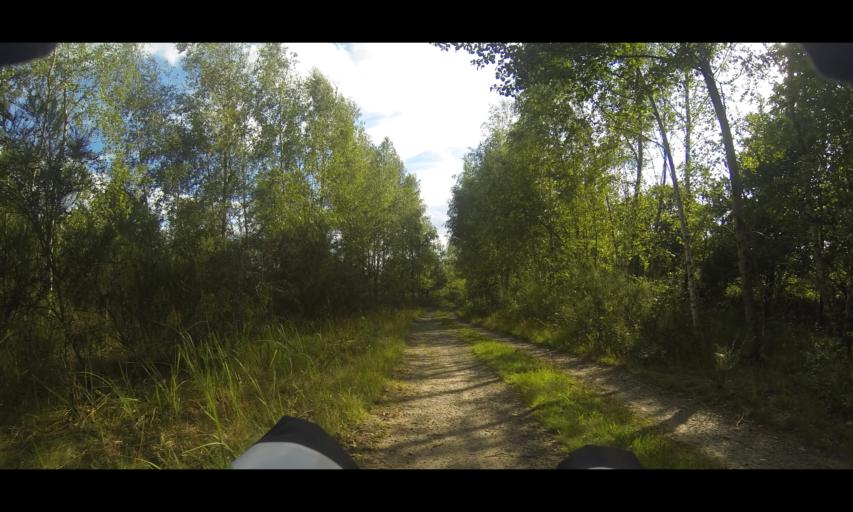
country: DE
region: Saxony
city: Konigsbruck
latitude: 51.2879
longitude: 13.8835
